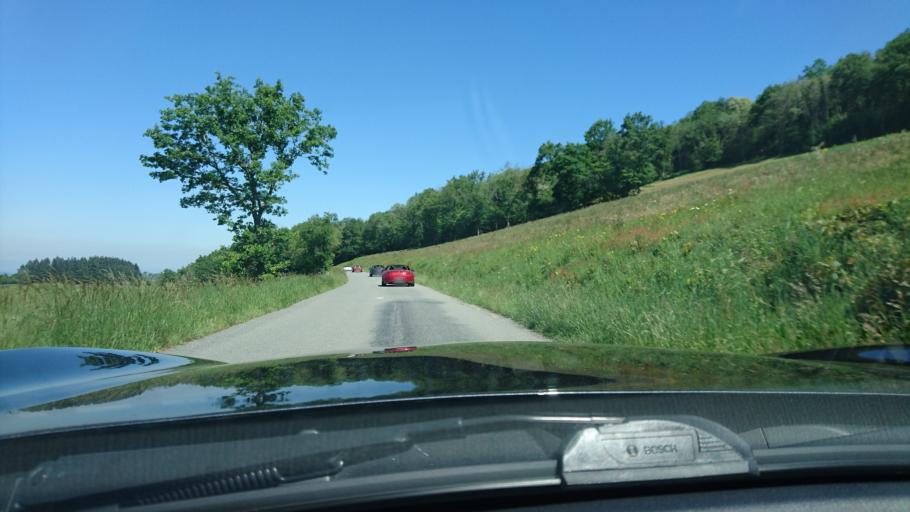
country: FR
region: Rhone-Alpes
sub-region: Departement de la Loire
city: Violay
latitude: 45.8806
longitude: 4.3354
